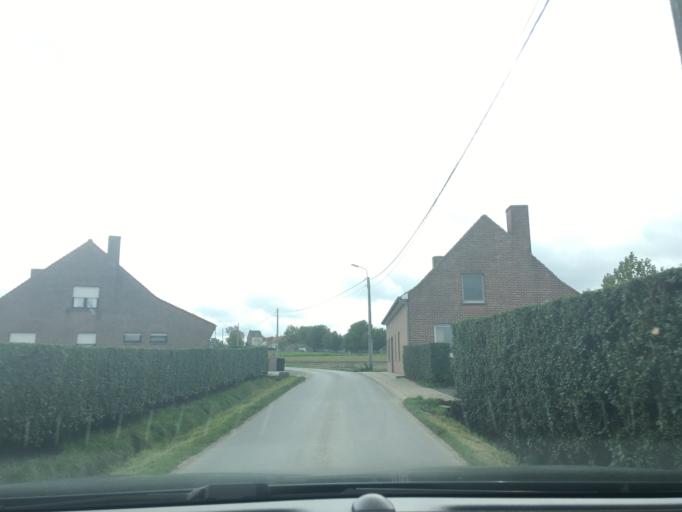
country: BE
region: Flanders
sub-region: Provincie West-Vlaanderen
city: Moorslede
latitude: 50.8978
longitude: 3.0559
